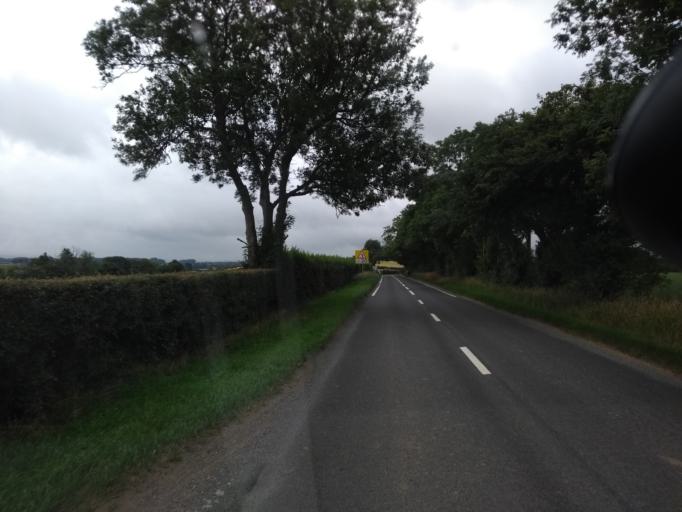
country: GB
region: England
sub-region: Somerset
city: Merriott
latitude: 50.9197
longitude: -2.7742
